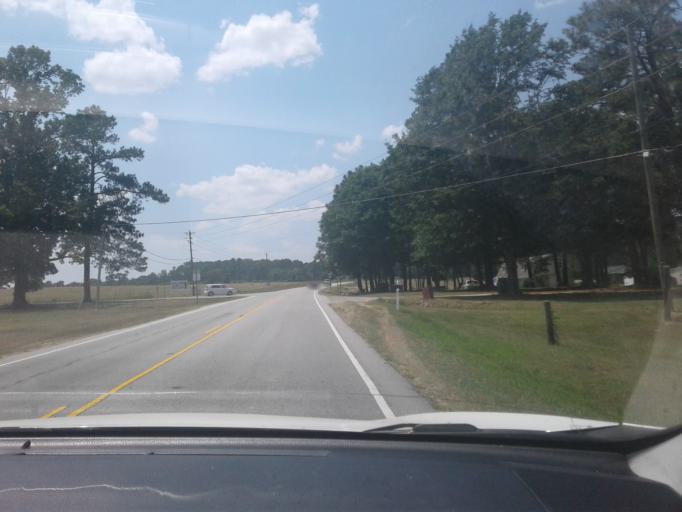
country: US
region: North Carolina
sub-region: Johnston County
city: Benson
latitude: 35.3897
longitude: -78.5801
